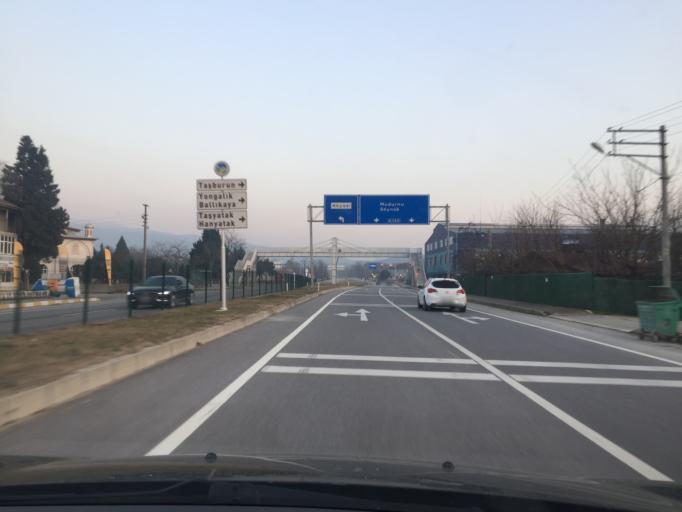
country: TR
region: Sakarya
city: Akyazi
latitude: 40.6353
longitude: 30.6259
